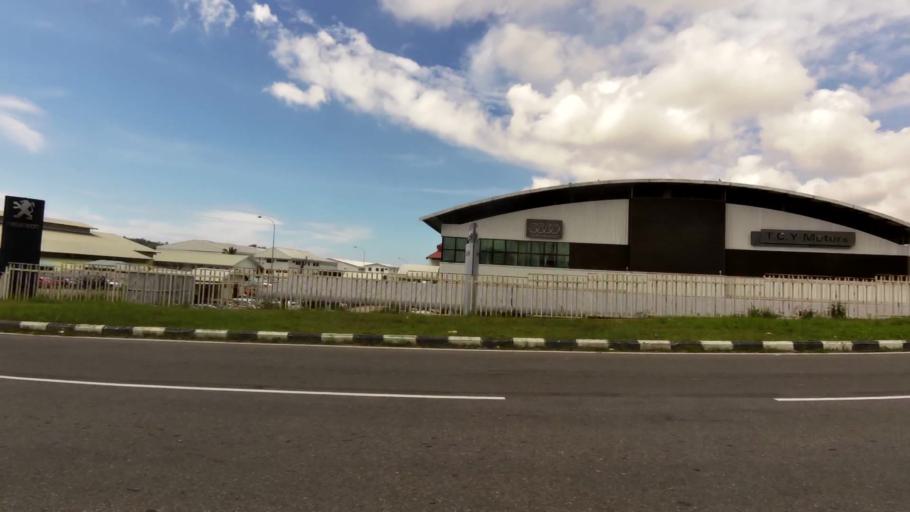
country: BN
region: Brunei and Muara
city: Bandar Seri Begawan
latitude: 4.9803
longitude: 114.9561
